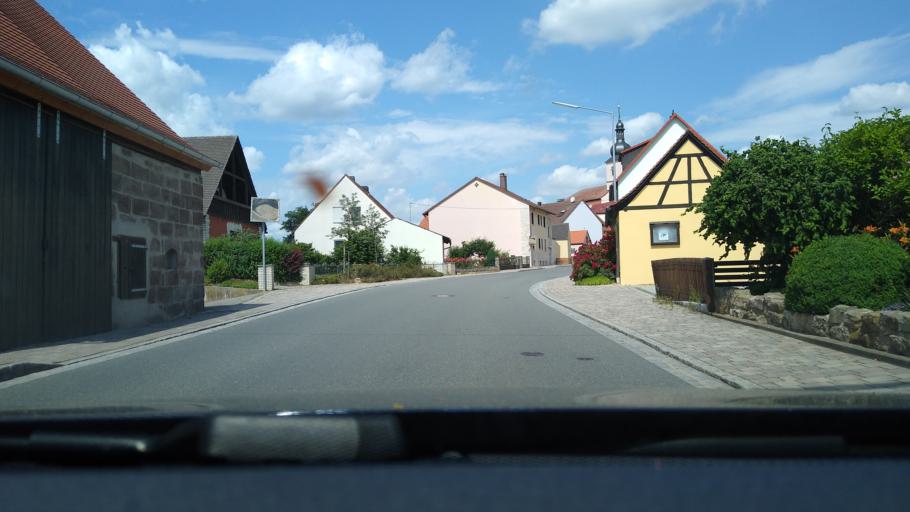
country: DE
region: Bavaria
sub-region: Regierungsbezirk Mittelfranken
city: Trautskirchen
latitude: 49.4557
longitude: 10.5950
